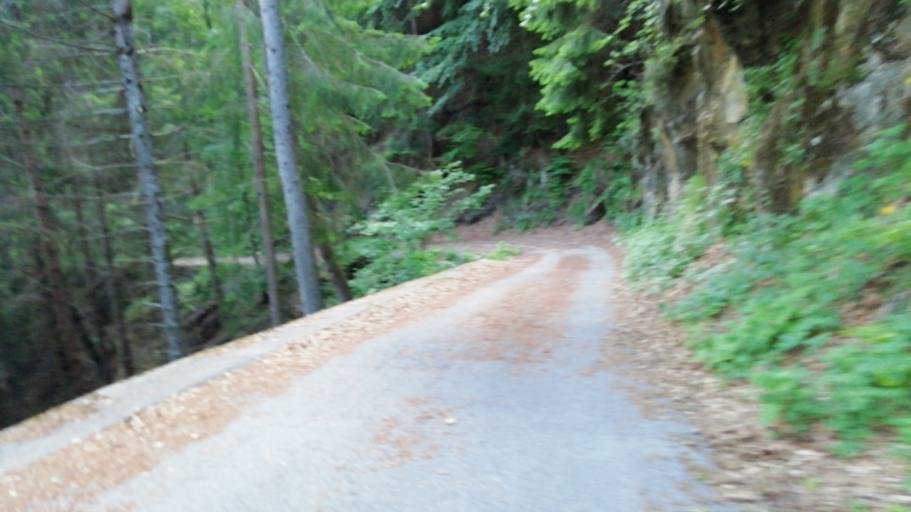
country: IT
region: Veneto
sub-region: Provincia di Belluno
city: Valle di Cadore
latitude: 46.4228
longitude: 12.3224
